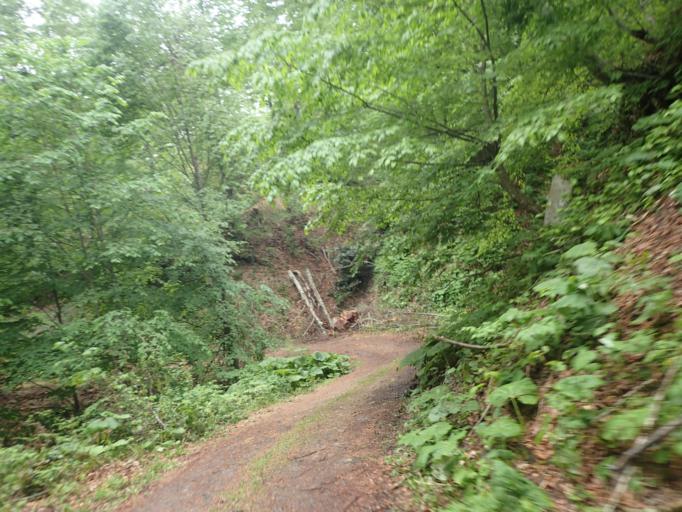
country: TR
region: Ordu
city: Akkus
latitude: 40.8695
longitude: 37.0820
